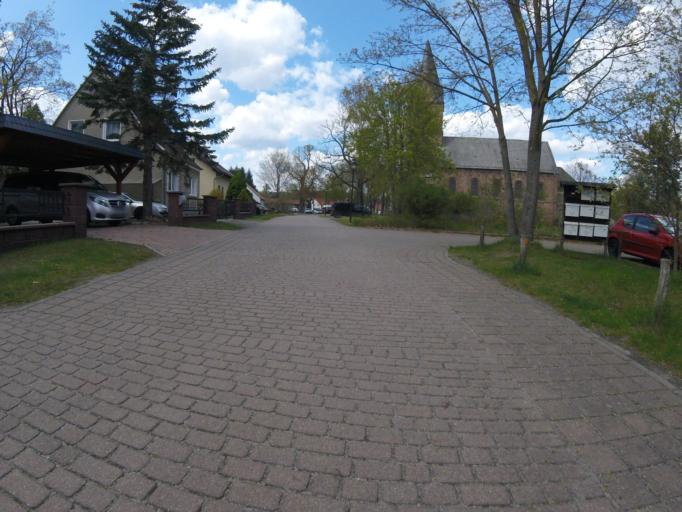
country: DE
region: Brandenburg
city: Munchehofe
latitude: 52.2223
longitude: 13.7667
